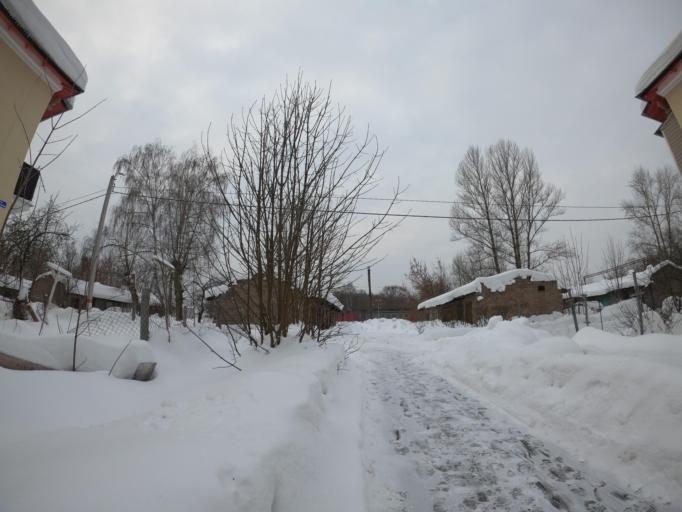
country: RU
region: Moskovskaya
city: Elektrogorsk
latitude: 55.8823
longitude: 38.7891
